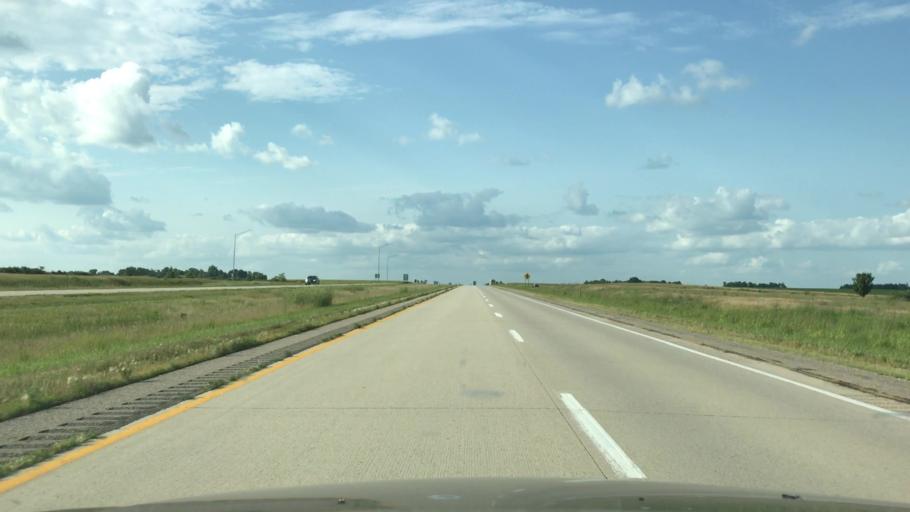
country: US
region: Iowa
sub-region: Osceola County
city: Sibley
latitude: 43.4058
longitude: -95.7171
